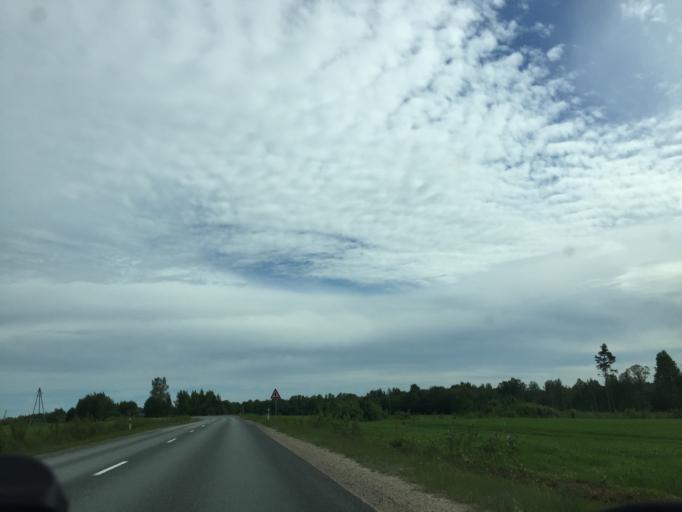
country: LV
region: Beverina
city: Murmuiza
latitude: 57.4635
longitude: 25.4155
